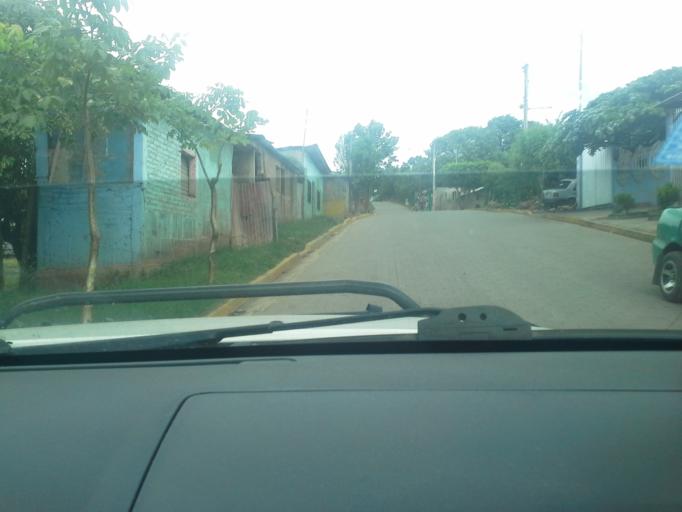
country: NI
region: Matagalpa
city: Ciudad Dario
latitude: 12.8542
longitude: -86.0924
